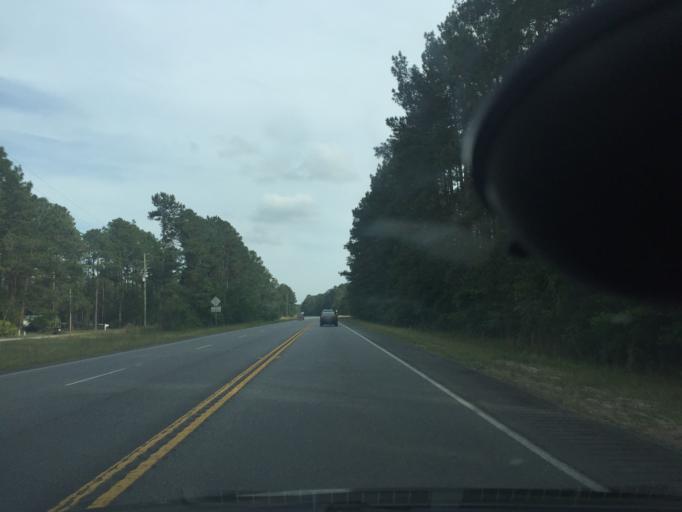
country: US
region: Georgia
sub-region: Chatham County
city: Bloomingdale
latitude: 32.0487
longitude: -81.3388
